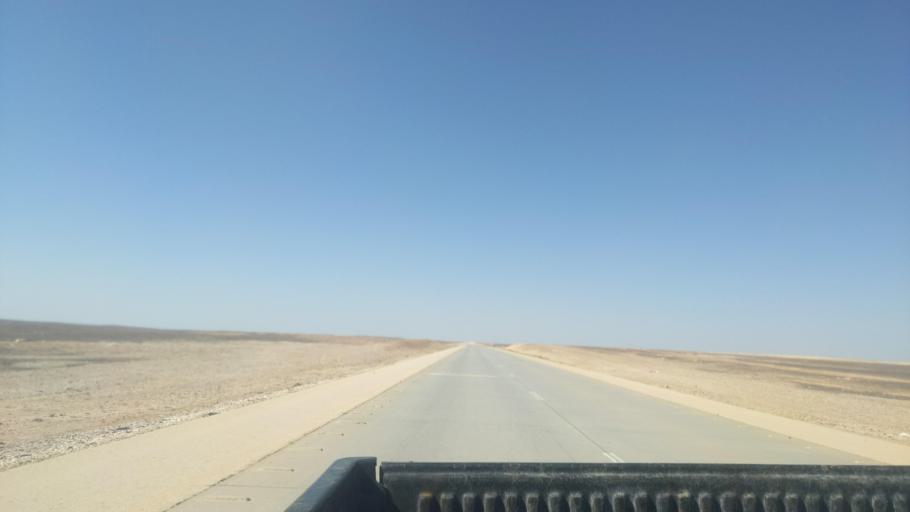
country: JO
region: Amman
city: Al Azraq ash Shamali
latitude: 31.4179
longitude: 36.7227
